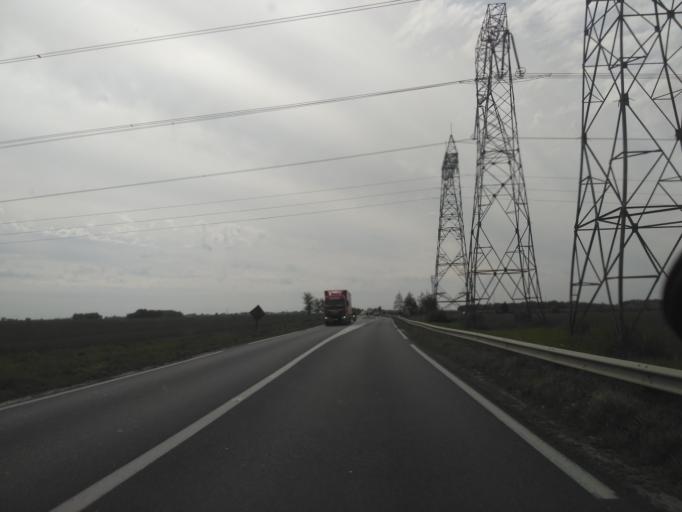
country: FR
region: Ile-de-France
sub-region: Departement de Seine-et-Marne
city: Solers
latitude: 48.6348
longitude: 2.7368
